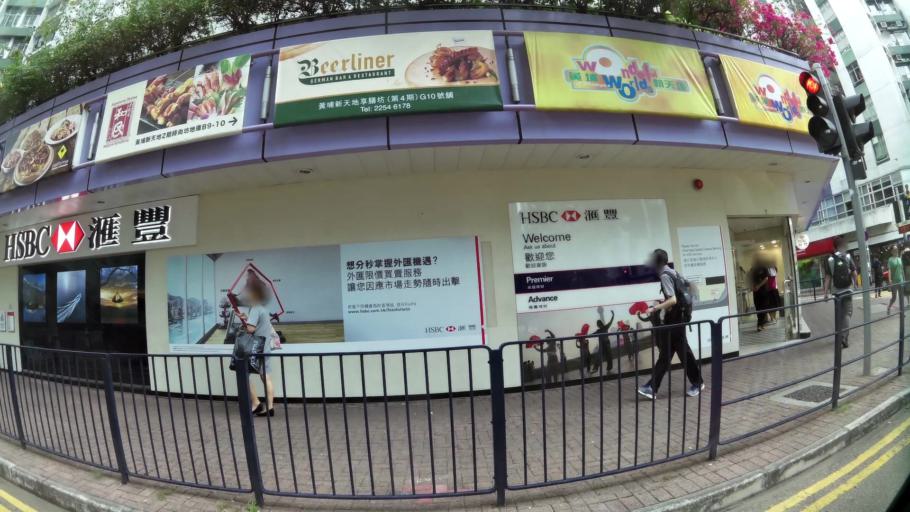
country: HK
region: Kowloon City
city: Kowloon
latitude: 22.3036
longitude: 114.1891
